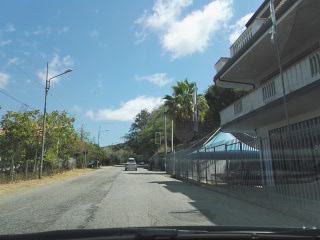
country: IT
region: Calabria
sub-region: Provincia di Vibo-Valentia
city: Ricadi
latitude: 38.6093
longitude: 15.8754
